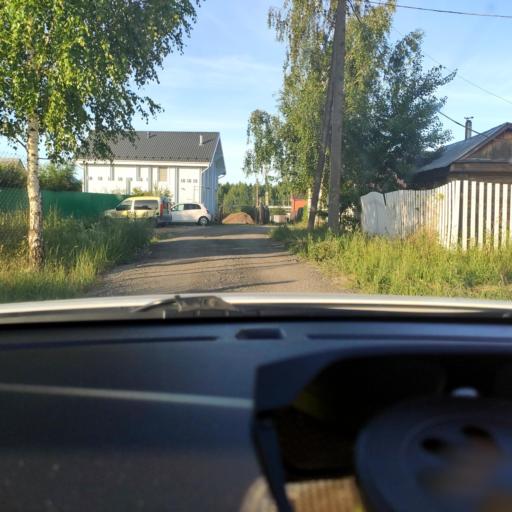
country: RU
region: Tatarstan
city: Stolbishchi
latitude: 55.6950
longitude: 49.1917
